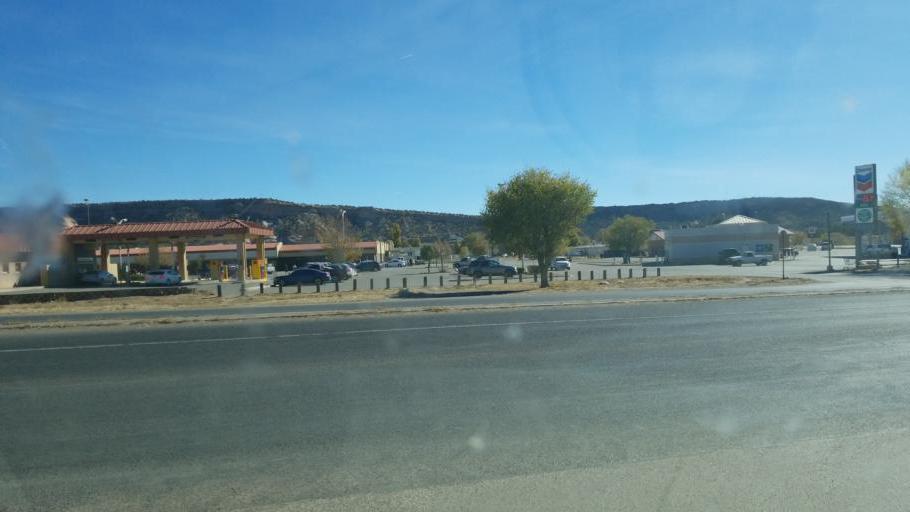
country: US
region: Arizona
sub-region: Apache County
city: Window Rock
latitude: 35.6647
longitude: -109.0576
